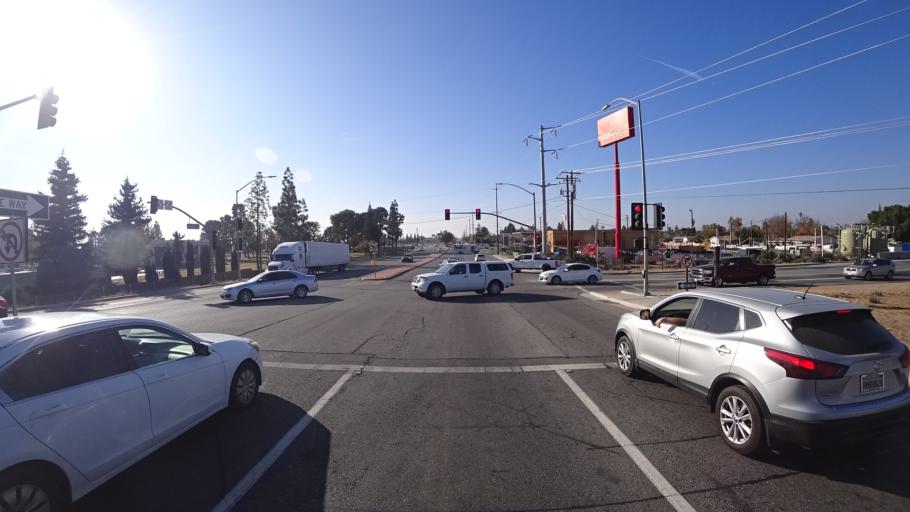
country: US
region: California
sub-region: Kern County
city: Greenfield
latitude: 35.2959
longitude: -119.0318
